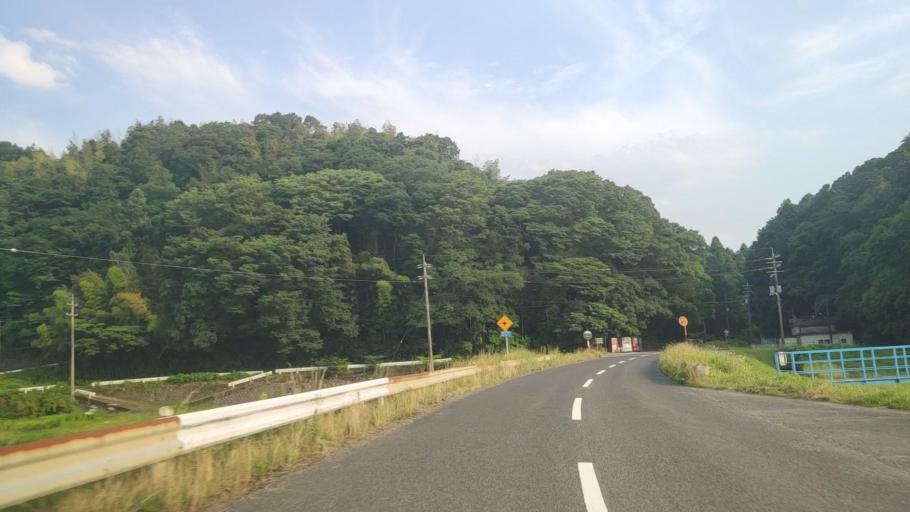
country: JP
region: Tottori
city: Kurayoshi
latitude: 35.4164
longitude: 133.7838
